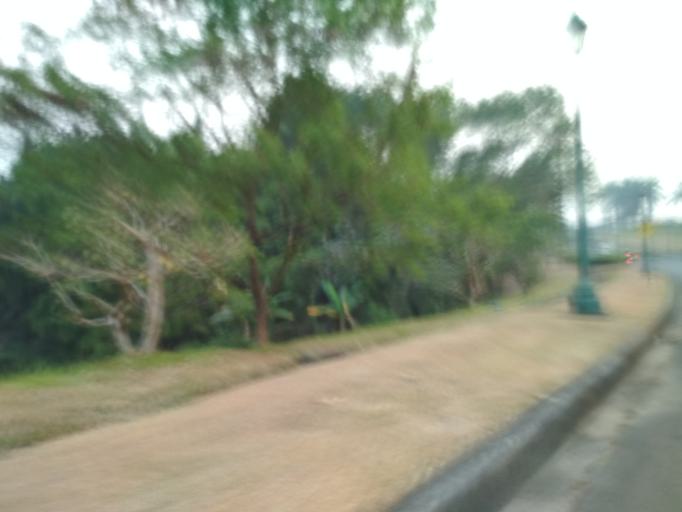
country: ID
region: West Java
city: Caringin
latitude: -6.6625
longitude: 106.8335
